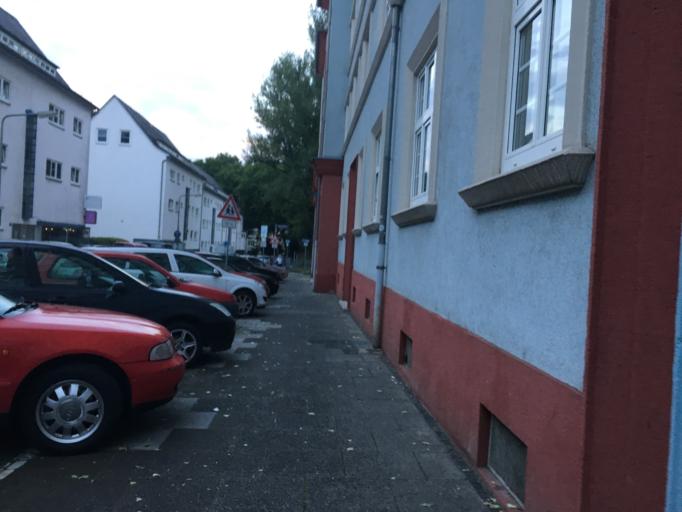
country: DE
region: Hesse
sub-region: Regierungsbezirk Darmstadt
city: Frankfurt am Main
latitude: 50.1275
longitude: 8.7135
